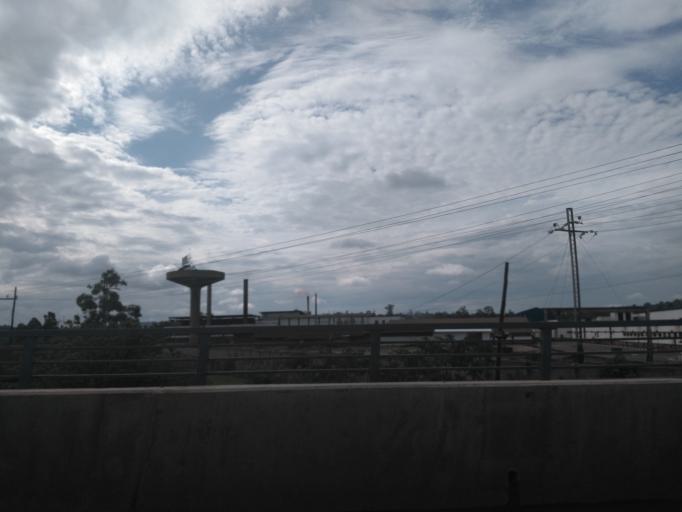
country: UG
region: Eastern Region
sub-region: Jinja District
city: Jinja
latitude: 0.4382
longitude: 33.1866
